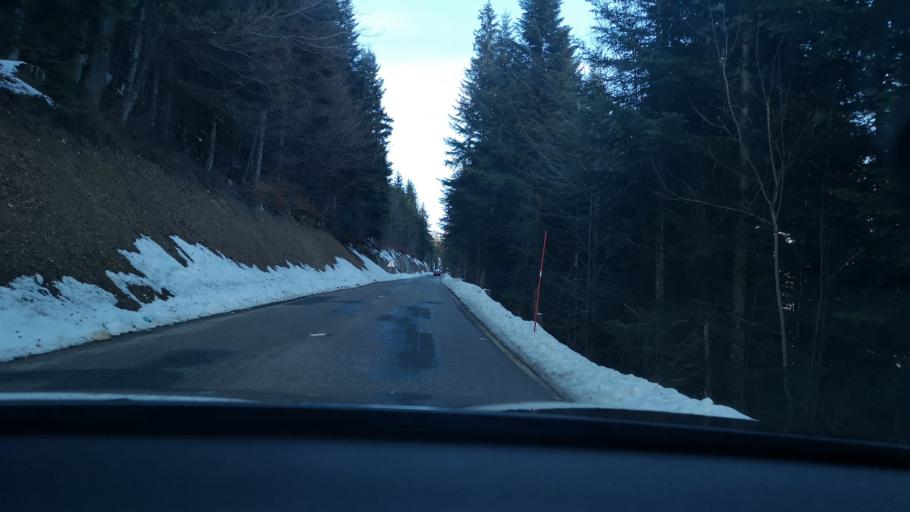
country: FR
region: Franche-Comte
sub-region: Departement du Doubs
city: Gilley
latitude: 46.9923
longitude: 6.5321
